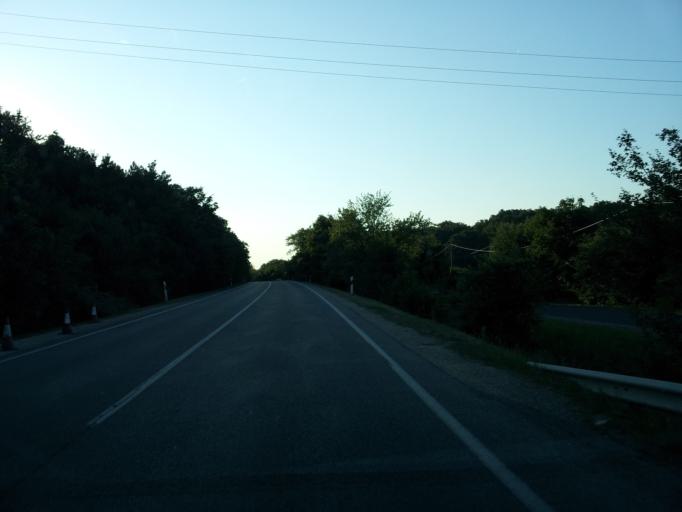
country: HU
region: Fejer
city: Szarliget
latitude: 47.5285
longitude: 18.4639
